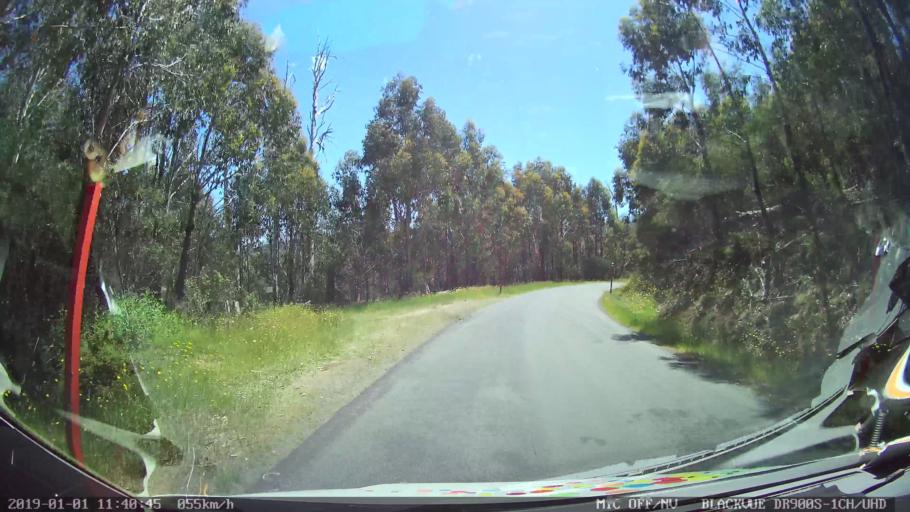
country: AU
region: New South Wales
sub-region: Snowy River
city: Jindabyne
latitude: -35.9179
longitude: 148.3878
